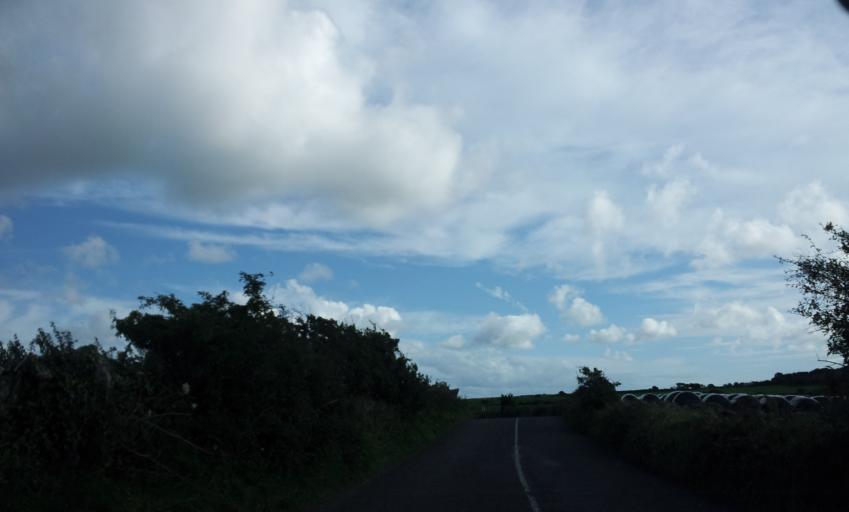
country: IE
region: Connaught
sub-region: County Galway
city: Bearna
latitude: 53.0501
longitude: -9.1431
